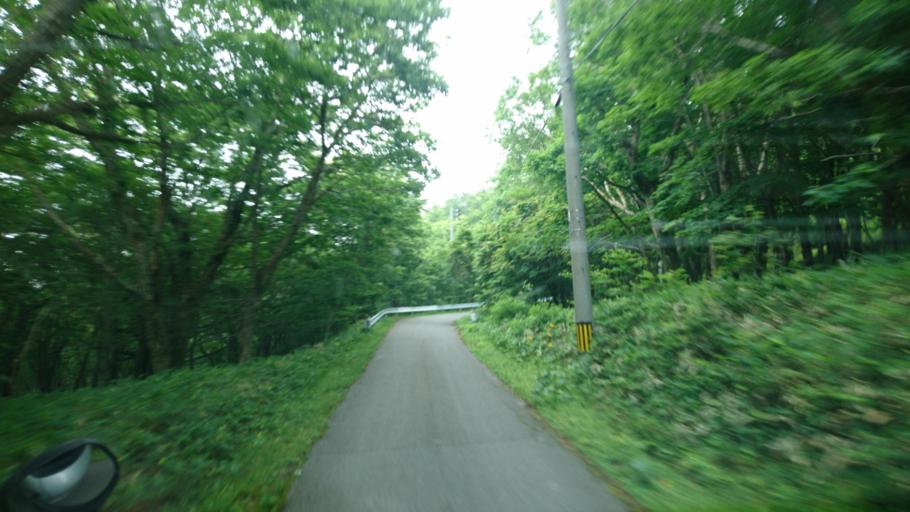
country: JP
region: Iwate
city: Ofunato
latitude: 39.1610
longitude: 141.7537
